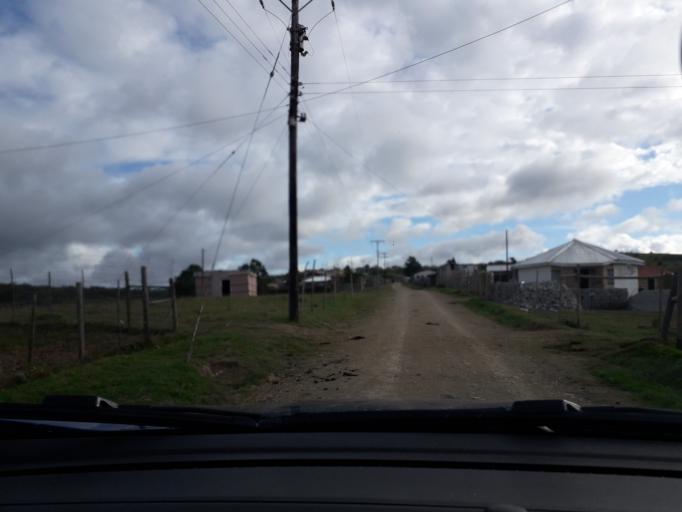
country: ZA
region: Eastern Cape
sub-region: Buffalo City Metropolitan Municipality
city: East London
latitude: -32.8041
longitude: 27.9635
